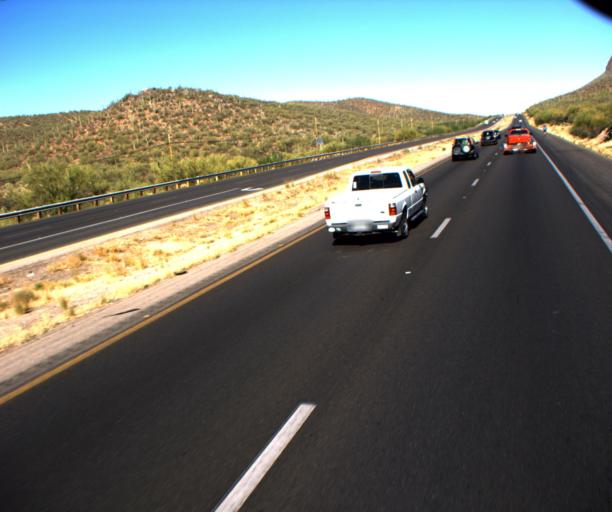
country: US
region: Arizona
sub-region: Pima County
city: Drexel Heights
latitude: 32.1768
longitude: -111.0292
